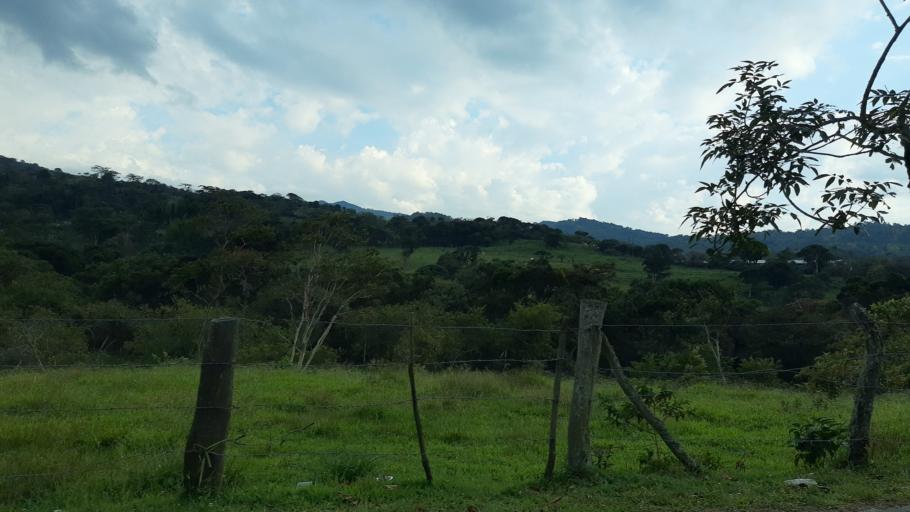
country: CO
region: Boyaca
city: Moniquira
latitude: 5.8424
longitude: -73.5844
